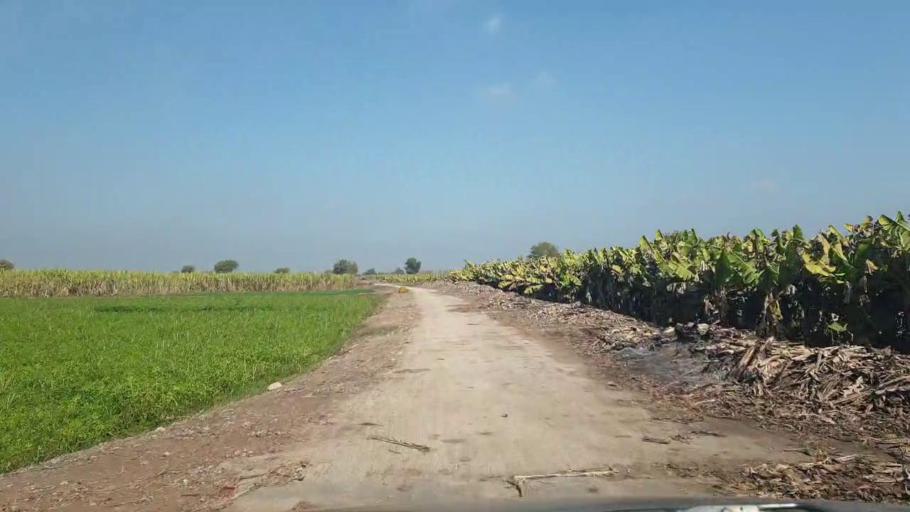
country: PK
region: Sindh
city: Shahdadpur
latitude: 25.9167
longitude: 68.5858
